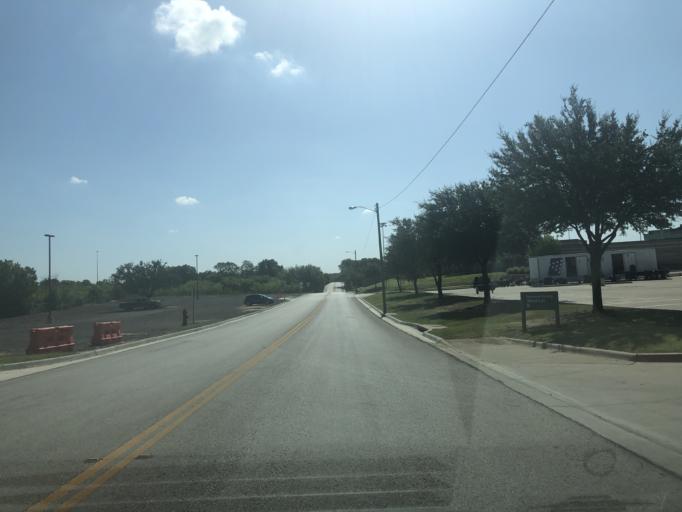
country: US
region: Texas
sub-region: Dallas County
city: Grand Prairie
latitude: 32.7560
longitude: -97.0042
